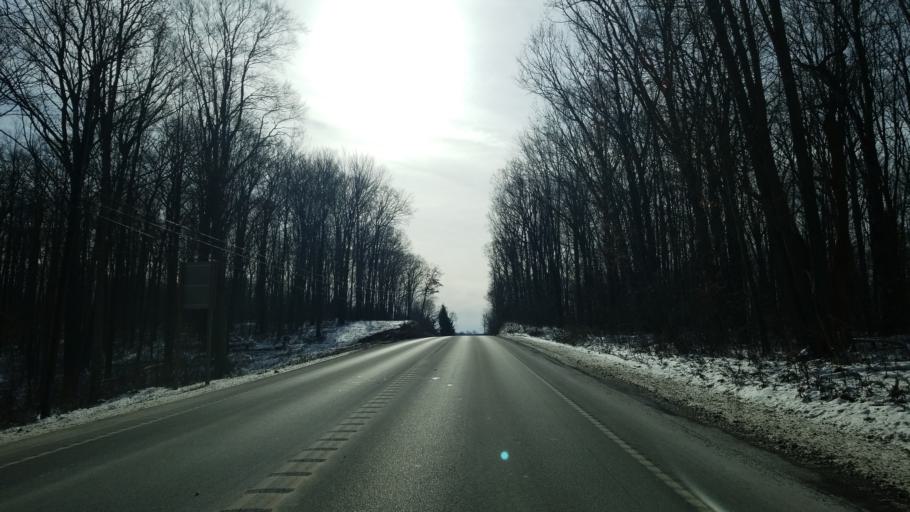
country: US
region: Pennsylvania
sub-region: Clearfield County
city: Treasure Lake
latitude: 41.1804
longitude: -78.5501
